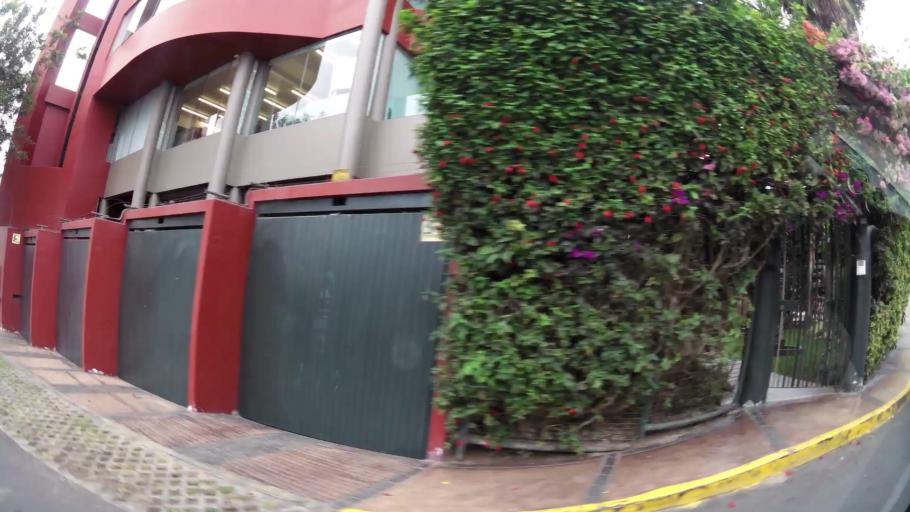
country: PE
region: Lima
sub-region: Lima
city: Surco
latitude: -12.1673
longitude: -77.0336
